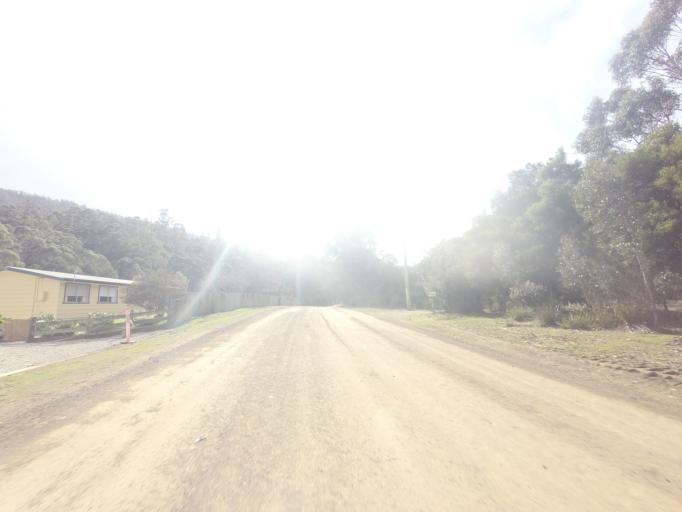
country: AU
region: Tasmania
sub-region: Huon Valley
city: Huonville
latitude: -43.0684
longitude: 147.0882
